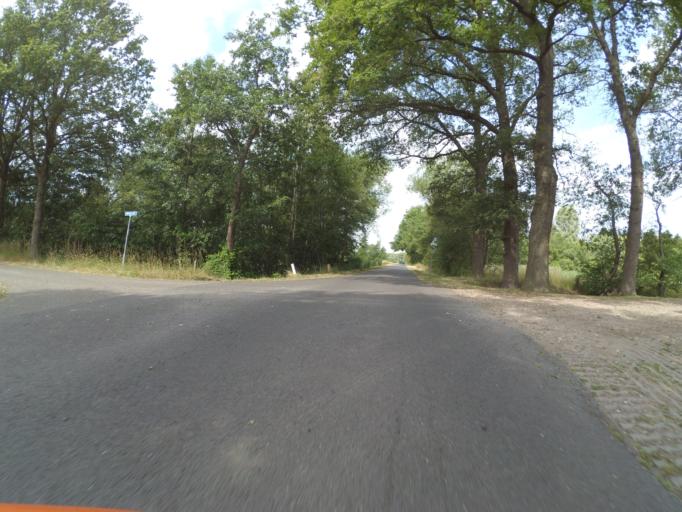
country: NL
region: Overijssel
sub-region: Gemeente Hof van Twente
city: Diepenheim
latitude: 52.1752
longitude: 6.5544
